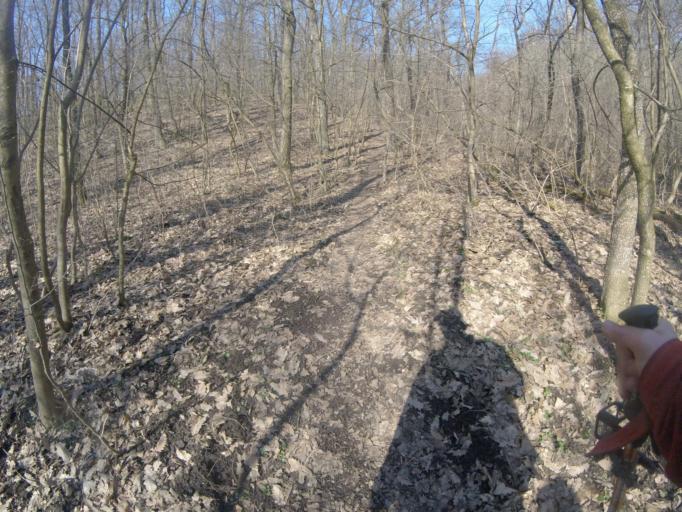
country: HU
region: Komarom-Esztergom
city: Nyergesujfalu
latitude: 47.7291
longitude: 18.5734
